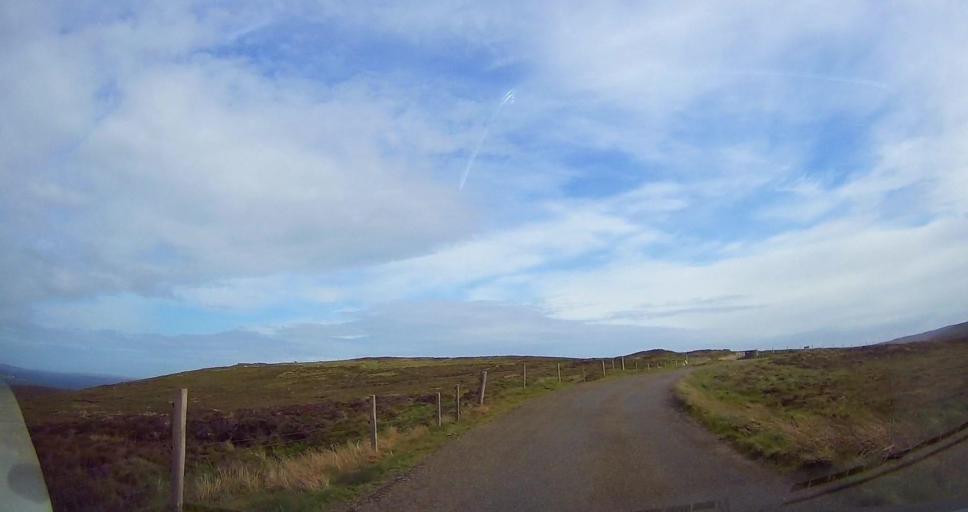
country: GB
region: Scotland
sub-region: Orkney Islands
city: Stromness
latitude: 58.8816
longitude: -3.2483
